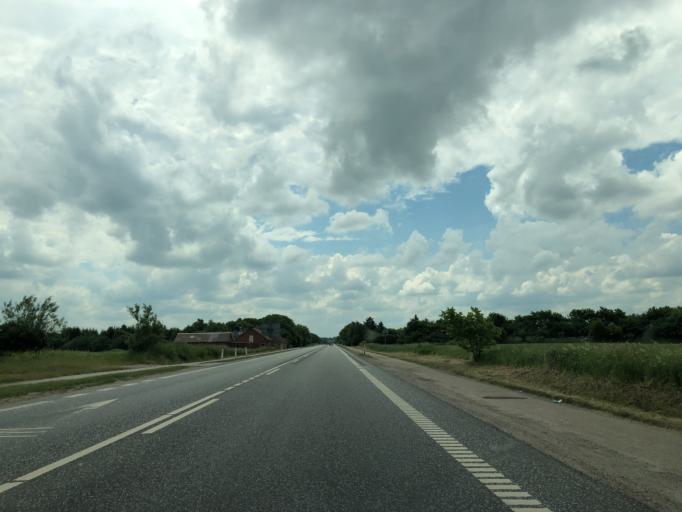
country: DK
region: Central Jutland
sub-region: Struer Kommune
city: Struer
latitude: 56.4721
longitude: 8.5862
